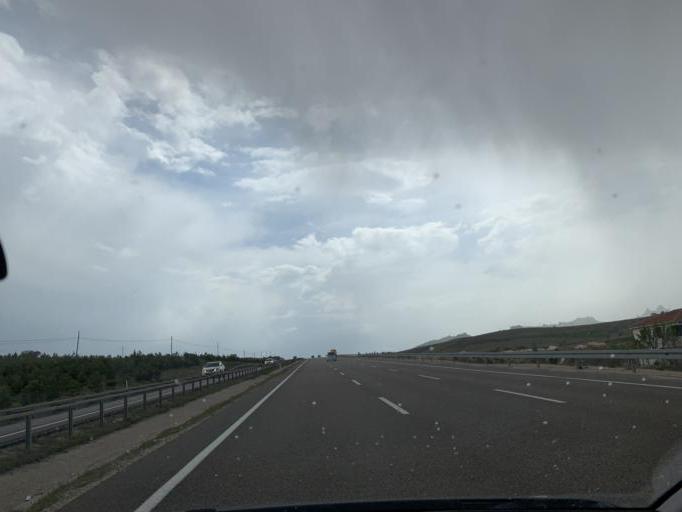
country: TR
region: Eskisehir
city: Sivrihisar
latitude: 39.4796
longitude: 31.5949
